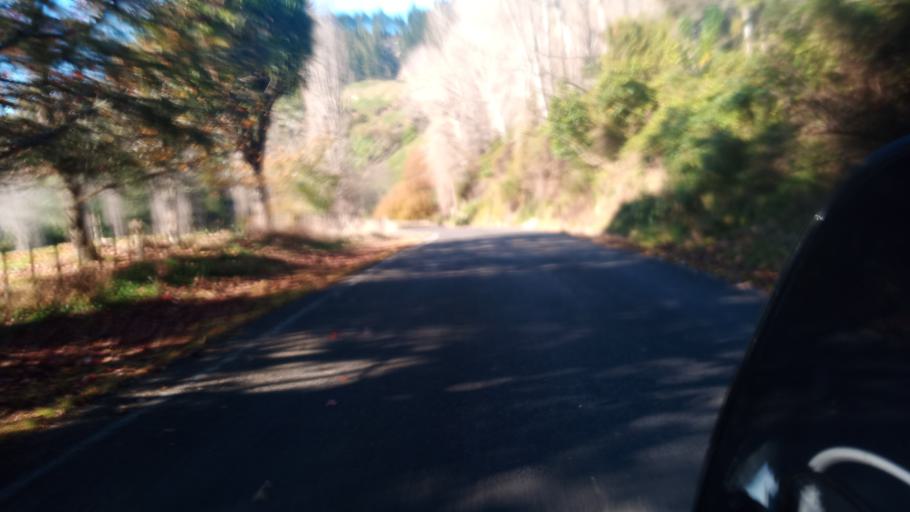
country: NZ
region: Hawke's Bay
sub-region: Wairoa District
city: Wairoa
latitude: -38.8192
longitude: 177.2942
